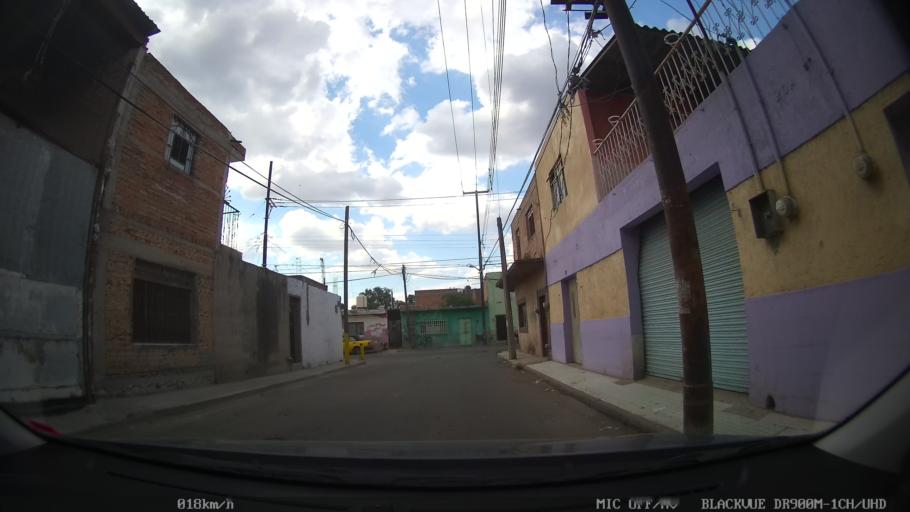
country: MX
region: Jalisco
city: Tlaquepaque
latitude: 20.6582
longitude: -103.2580
